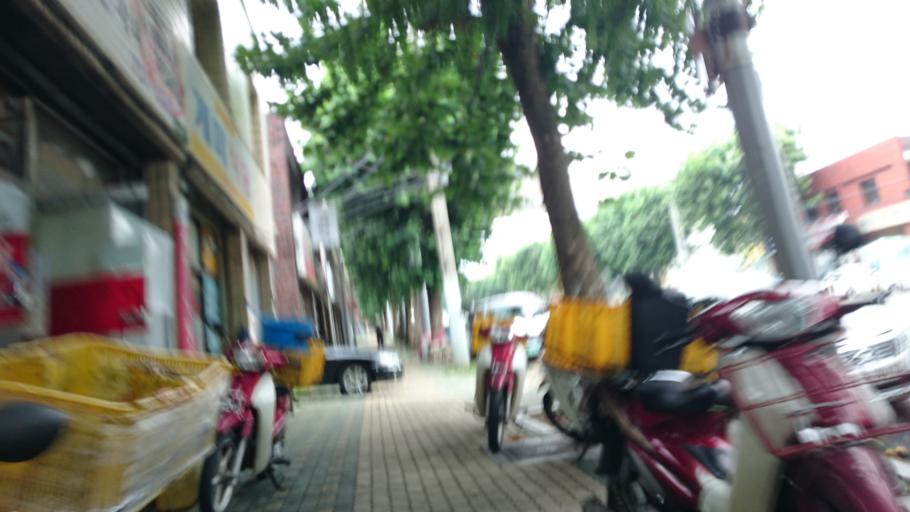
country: KR
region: Daegu
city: Daegu
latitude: 35.8688
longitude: 128.6473
